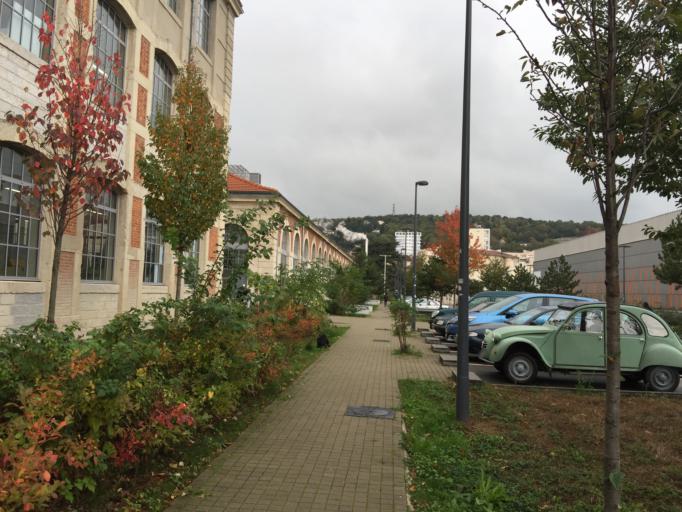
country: FR
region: Rhone-Alpes
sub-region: Departement de la Loire
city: Saint-Etienne
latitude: 45.4515
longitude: 4.3871
